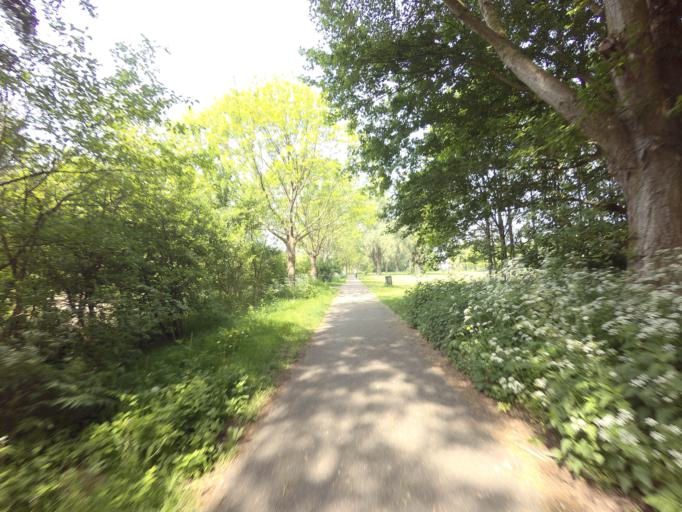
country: NL
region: South Holland
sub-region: Gemeente Hellevoetsluis
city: Nieuwenhoorn
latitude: 51.8297
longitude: 4.1705
